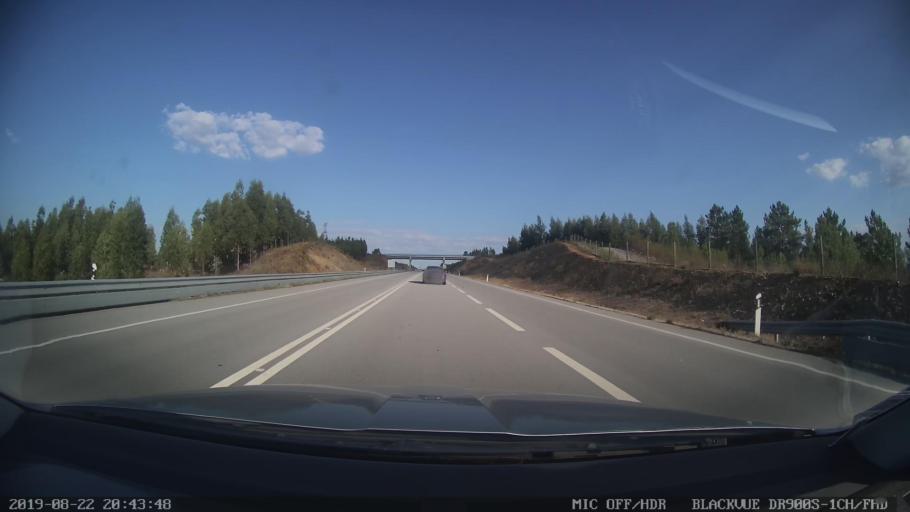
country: PT
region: Castelo Branco
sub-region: Proenca-A-Nova
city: Proenca-a-Nova
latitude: 39.7014
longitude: -7.8391
